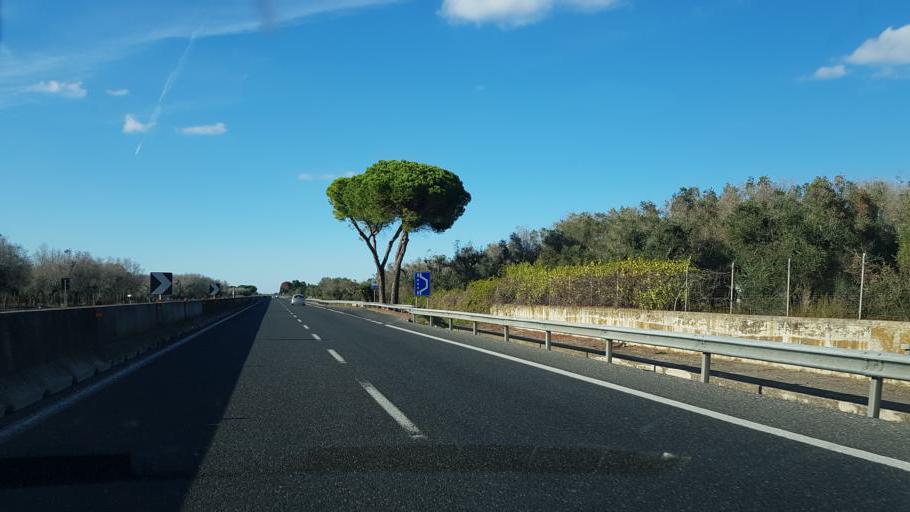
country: IT
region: Apulia
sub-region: Provincia di Brindisi
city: Torchiarolo
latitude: 40.4701
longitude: 18.0514
